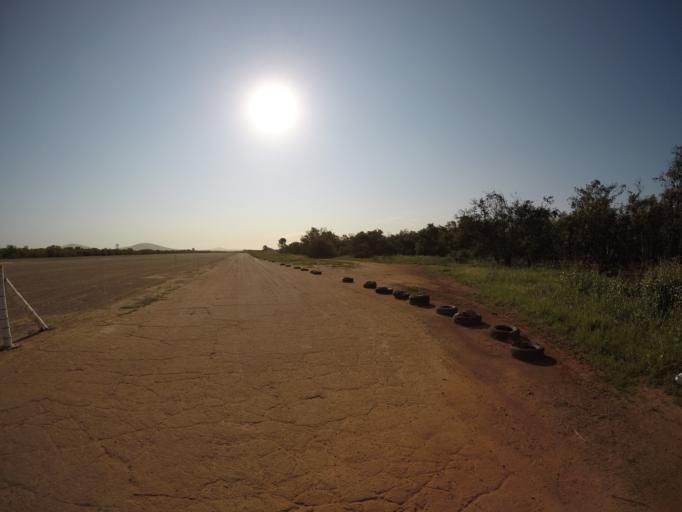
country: ZA
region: Western Cape
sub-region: City of Cape Town
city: Kraaifontein
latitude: -33.7735
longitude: 18.7469
